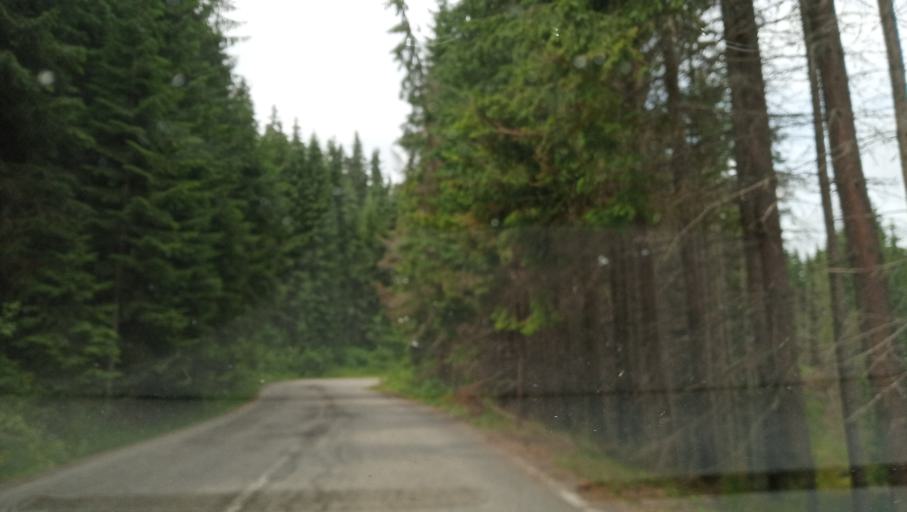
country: RO
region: Valcea
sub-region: Comuna Voineasa
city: Voineasa
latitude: 45.4284
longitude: 23.7425
